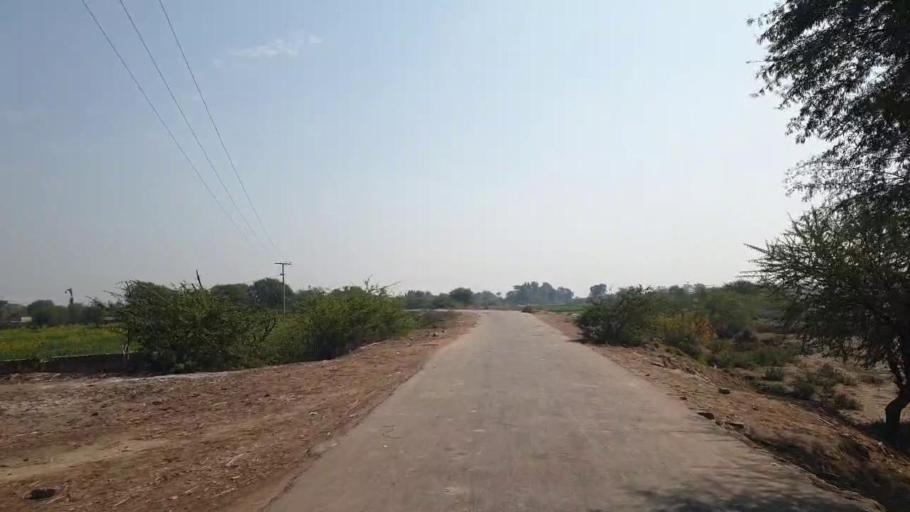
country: PK
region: Sindh
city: Chambar
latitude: 25.3395
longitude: 68.8513
